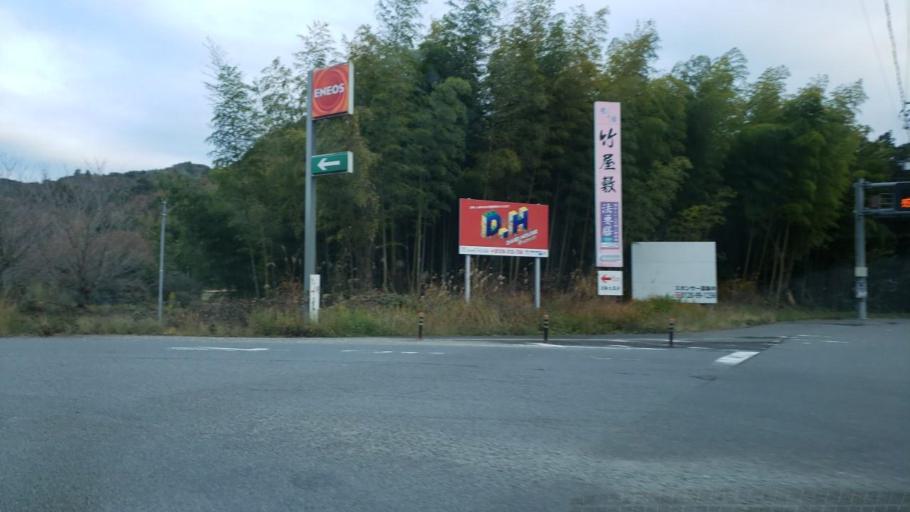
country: JP
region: Tokushima
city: Wakimachi
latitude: 34.1664
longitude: 134.1524
